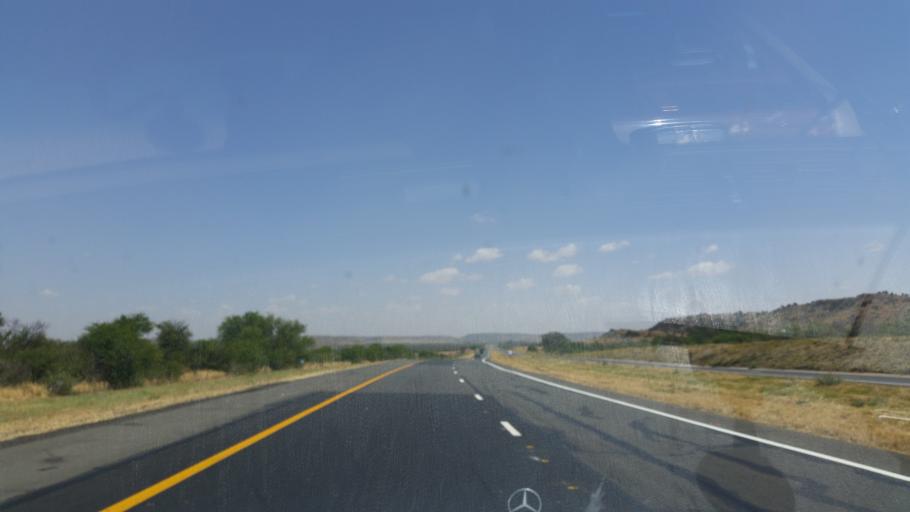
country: ZA
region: Orange Free State
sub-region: Mangaung Metropolitan Municipality
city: Bloemfontein
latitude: -28.9534
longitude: 26.3906
